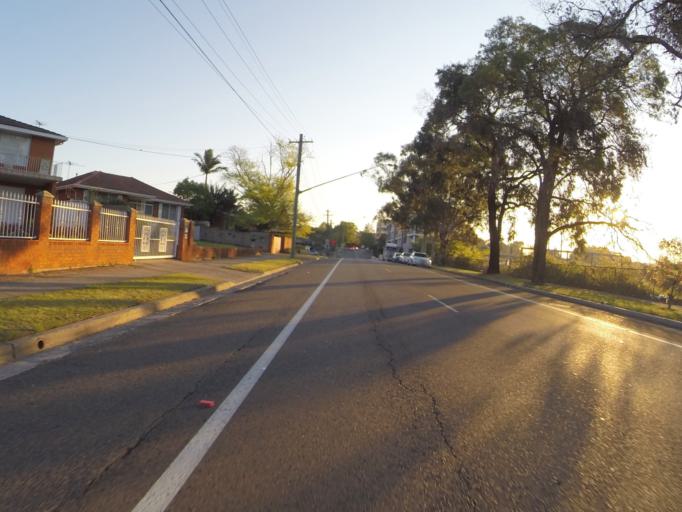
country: AU
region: New South Wales
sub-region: Rockdale
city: Bexley North
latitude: -33.9369
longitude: 151.1164
